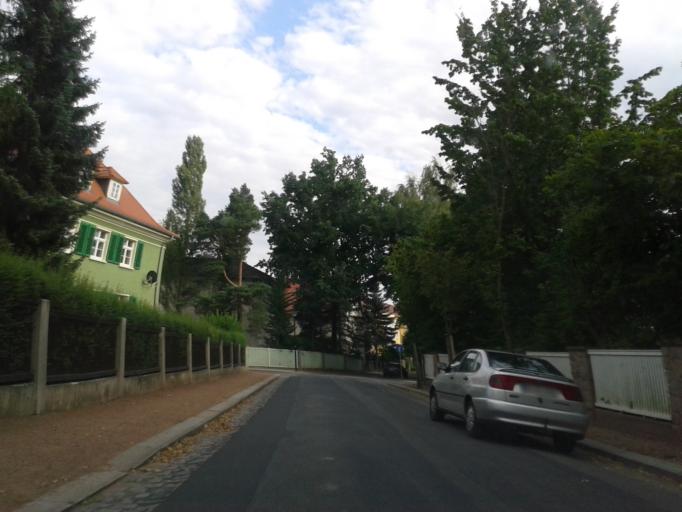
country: DE
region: Saxony
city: Radebeul
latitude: 51.1022
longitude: 13.6902
